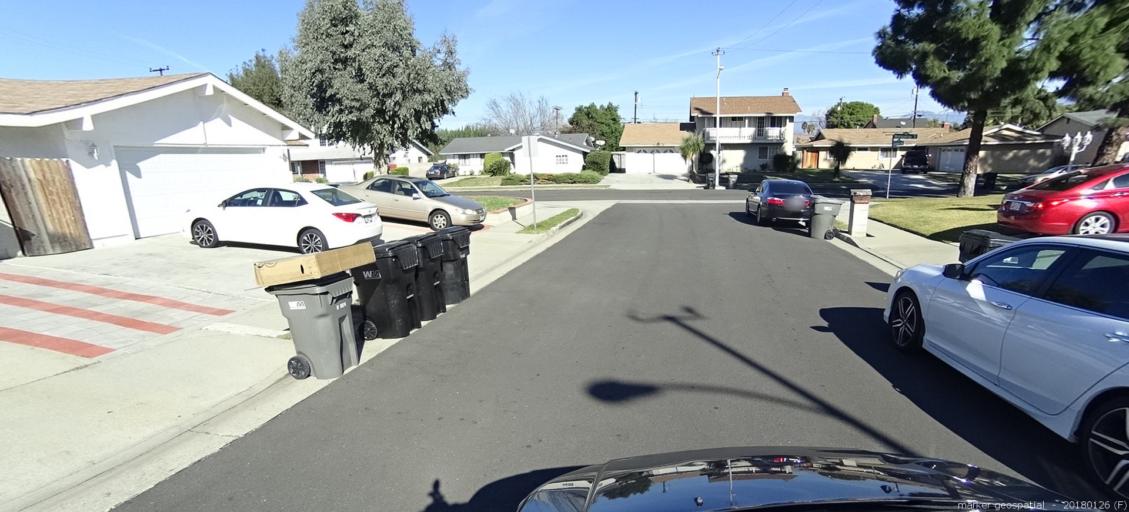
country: US
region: California
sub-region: Los Angeles County
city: Walnut
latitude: 34.0018
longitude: -117.8521
